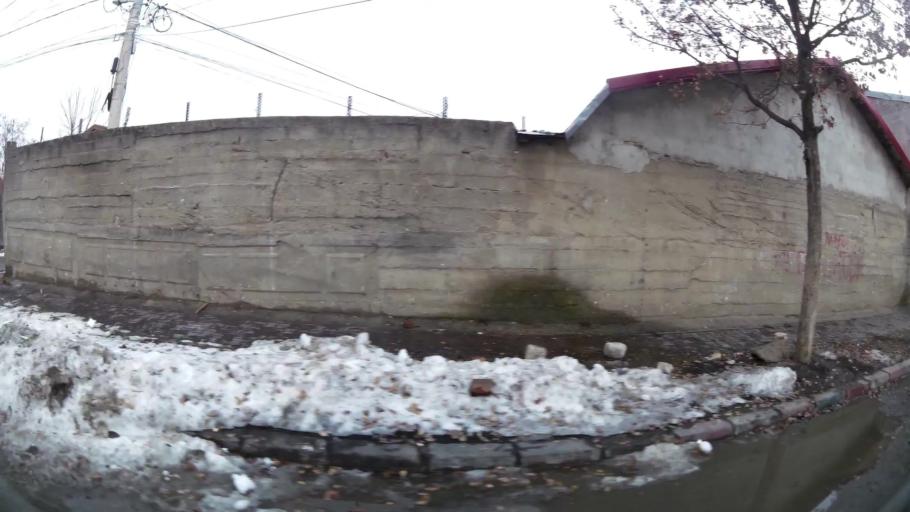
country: RO
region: Ilfov
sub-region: Voluntari City
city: Voluntari
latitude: 44.4809
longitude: 26.1837
